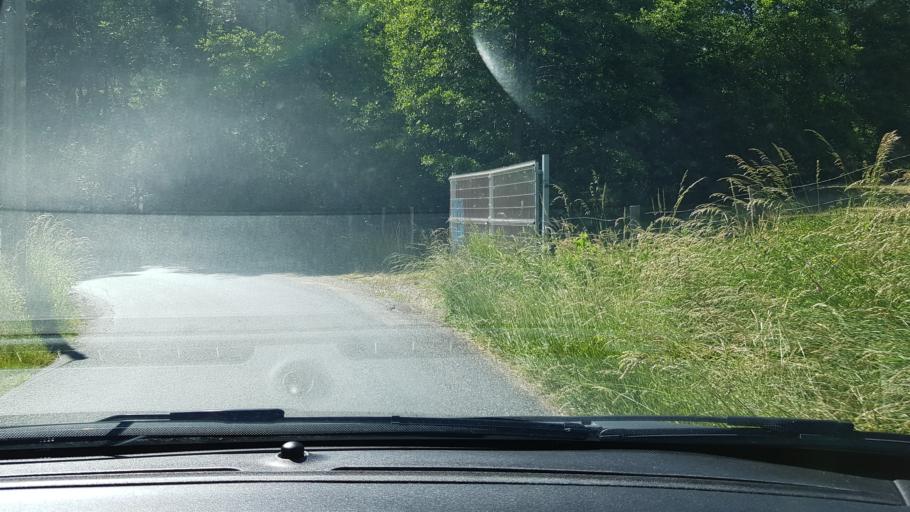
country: FR
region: Rhone-Alpes
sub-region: Departement du Rhone
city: Saint-Didier-sous-Riverie
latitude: 45.5958
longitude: 4.6063
